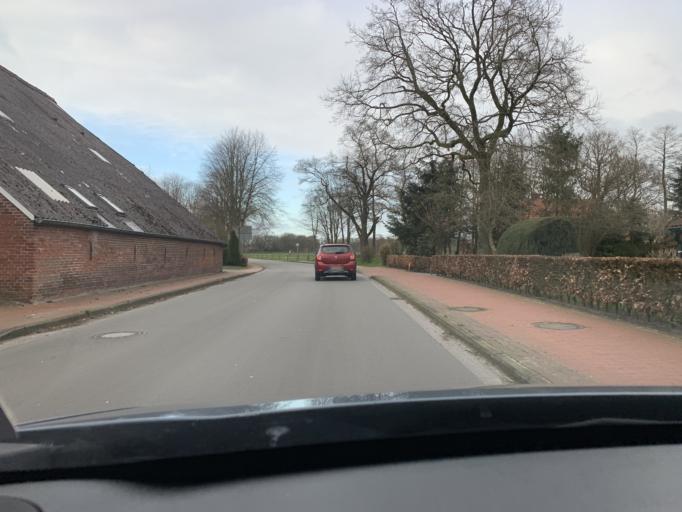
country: DE
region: Lower Saxony
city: Detern
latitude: 53.2557
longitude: 7.7109
